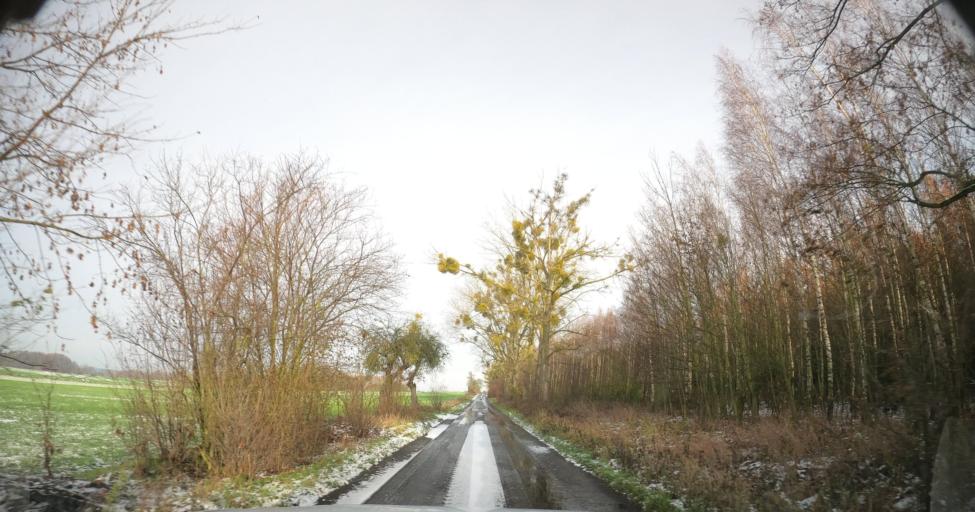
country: PL
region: West Pomeranian Voivodeship
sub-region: Powiat gryfinski
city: Mieszkowice
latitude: 52.7669
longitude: 14.4868
